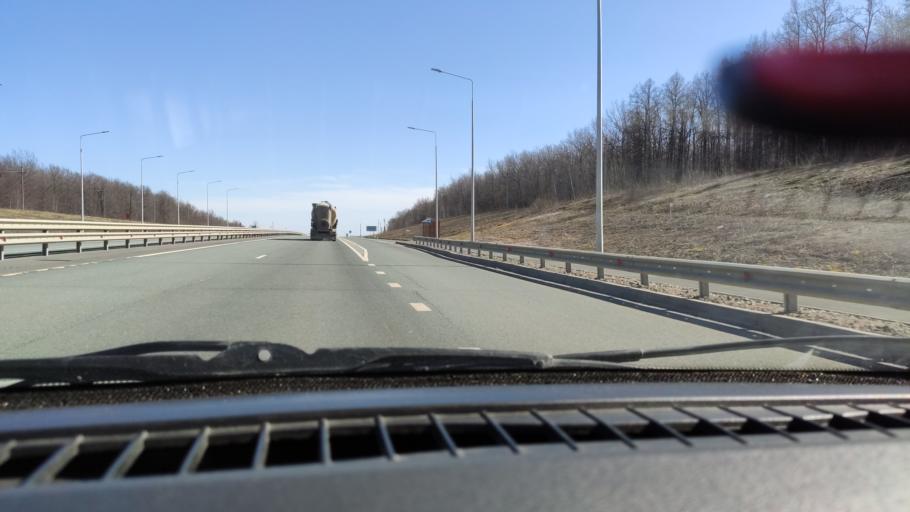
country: RU
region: Bashkortostan
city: Tolbazy
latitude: 54.0153
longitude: 55.9058
